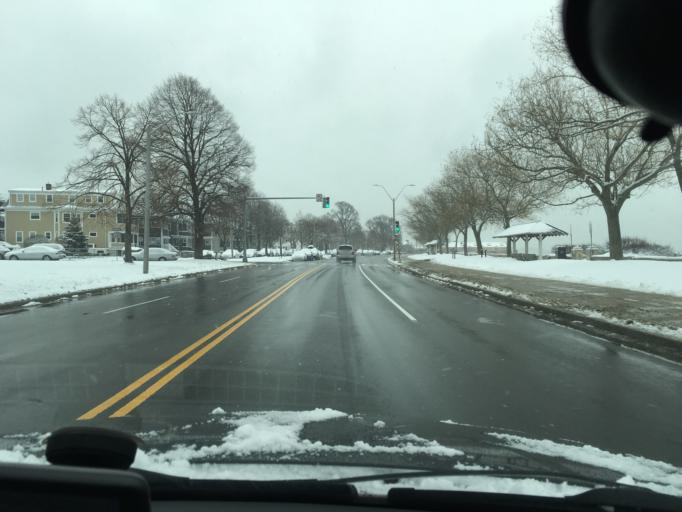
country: US
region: Massachusetts
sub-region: Suffolk County
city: South Boston
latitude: 42.3302
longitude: -71.0406
